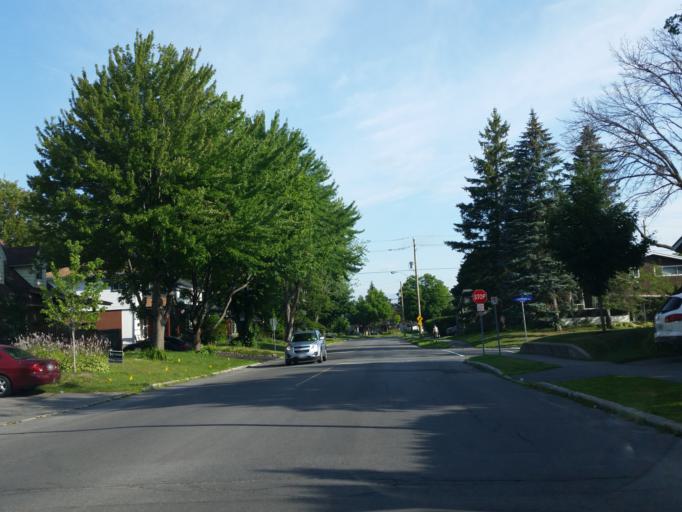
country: CA
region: Ontario
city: Ottawa
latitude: 45.3571
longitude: -75.7581
